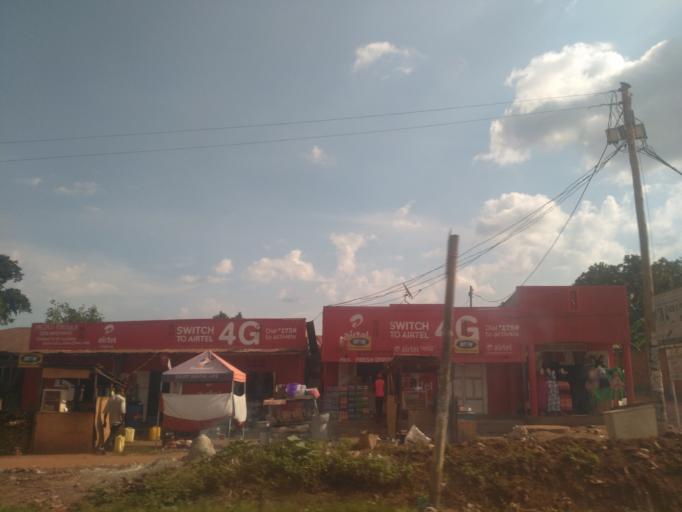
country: UG
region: Central Region
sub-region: Wakiso District
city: Kajansi
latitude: 0.2781
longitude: 32.4770
